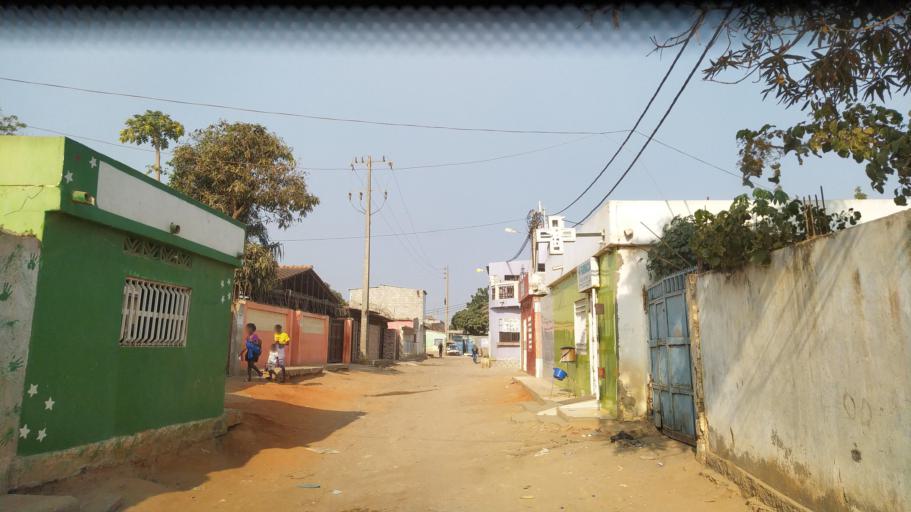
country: AO
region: Luanda
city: Luanda
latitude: -8.8717
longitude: 13.2085
